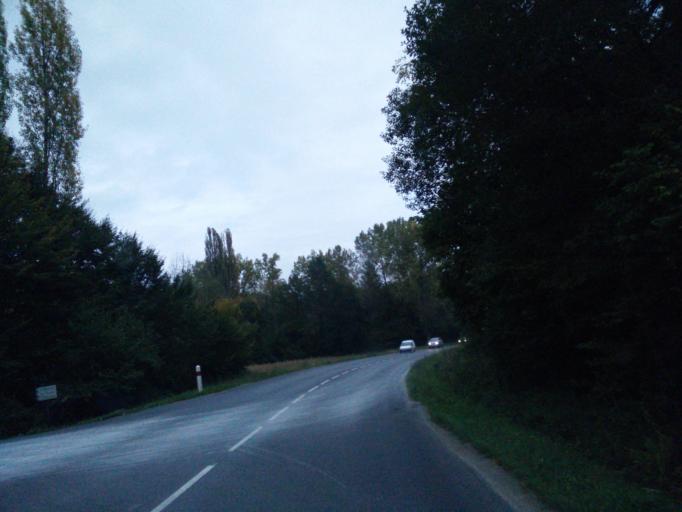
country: FR
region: Aquitaine
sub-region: Departement de la Dordogne
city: Carsac-Aillac
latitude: 44.8531
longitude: 1.2710
